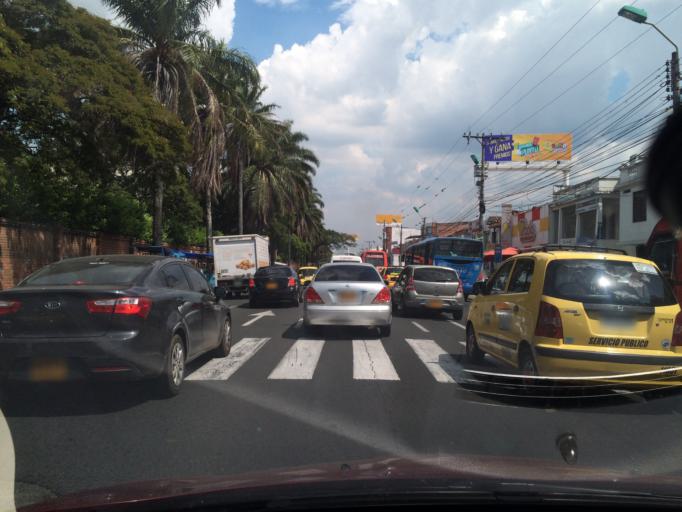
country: CO
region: Valle del Cauca
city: Cali
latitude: 3.4319
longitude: -76.5389
